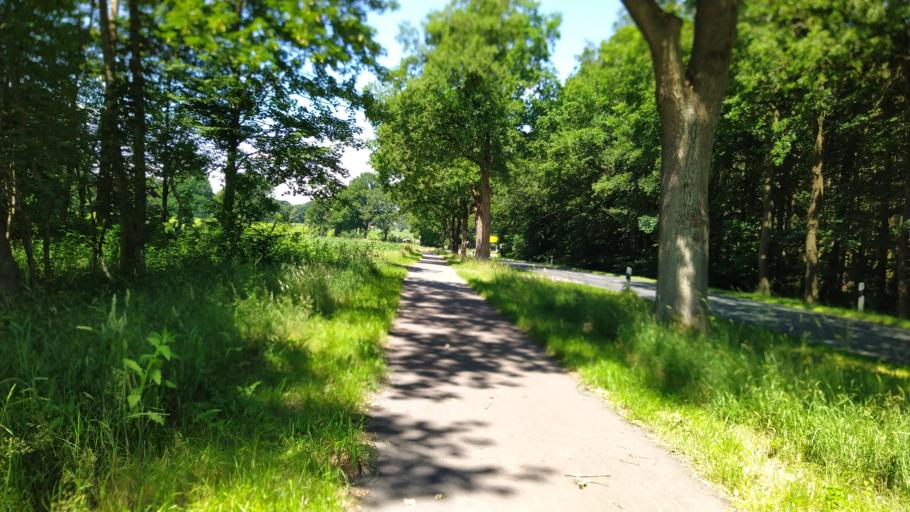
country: DE
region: Lower Saxony
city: Heinbockel
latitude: 53.5430
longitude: 9.3389
